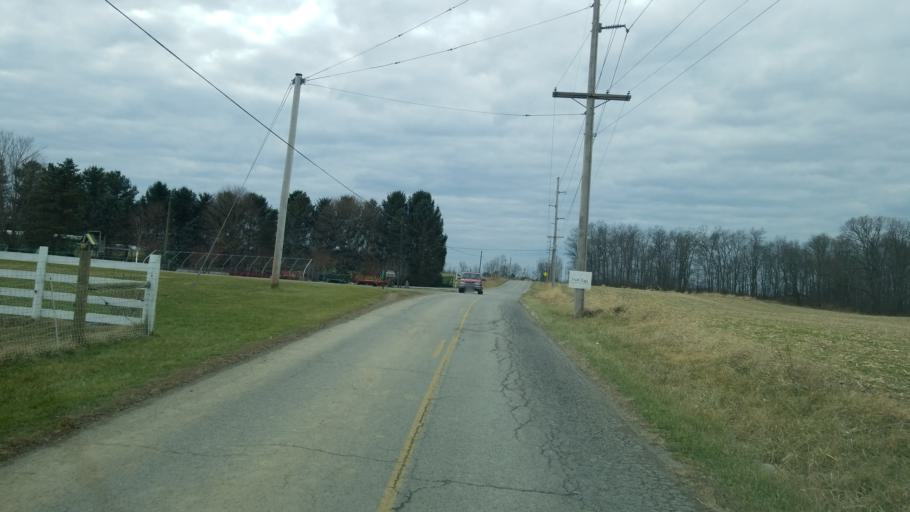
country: US
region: Ohio
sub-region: Highland County
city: Greenfield
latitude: 39.3310
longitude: -83.3233
